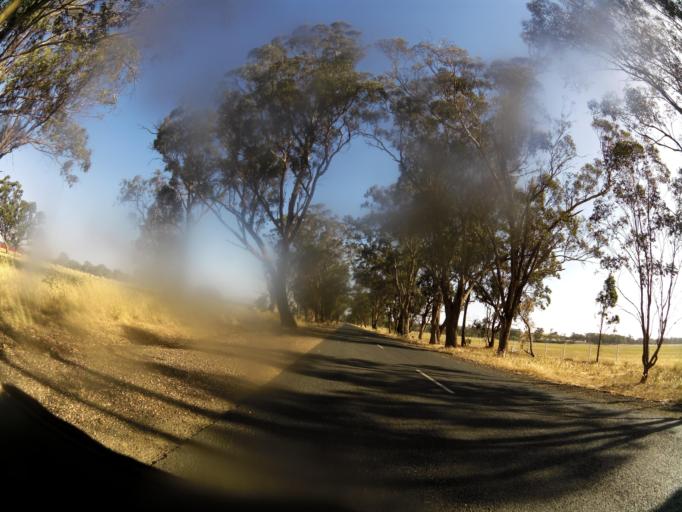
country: AU
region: Victoria
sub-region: Murrindindi
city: Kinglake West
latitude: -36.9793
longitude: 145.1106
